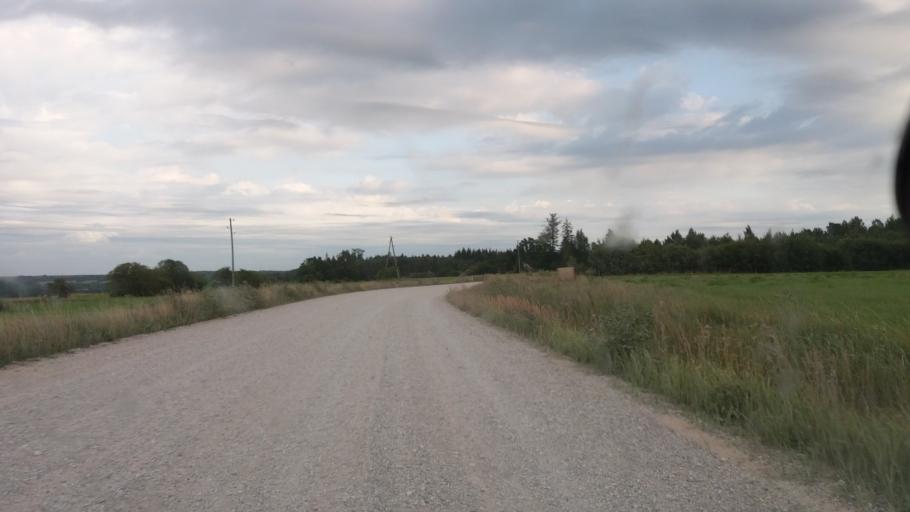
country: LV
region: Talsu Rajons
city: Sabile
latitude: 57.0252
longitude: 22.5850
